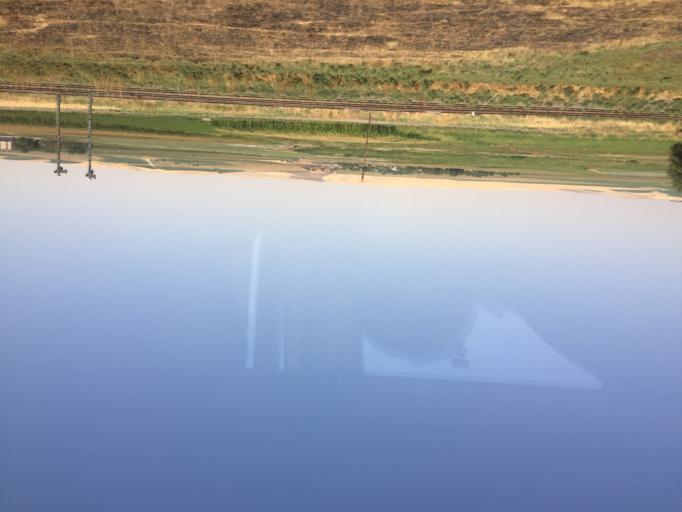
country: TR
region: Diyarbakir
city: Tepe
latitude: 37.8482
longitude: 40.8003
